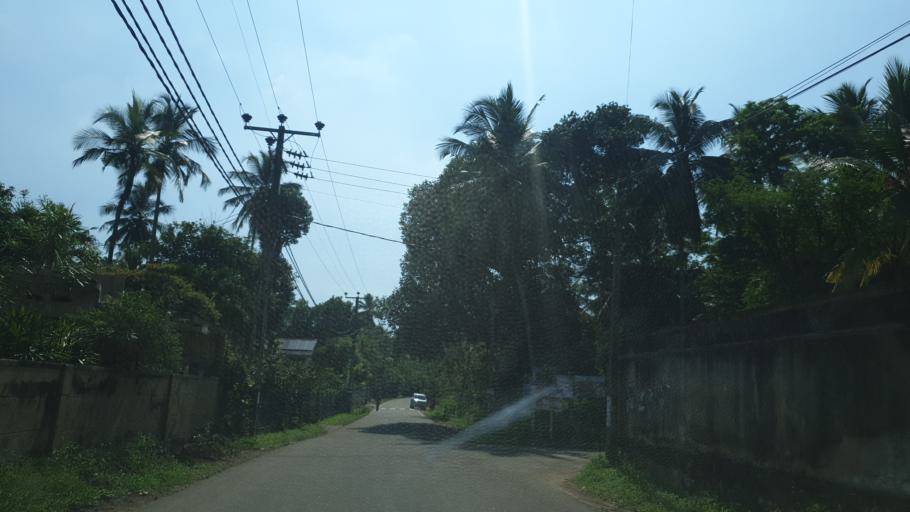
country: LK
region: Western
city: Moratuwa
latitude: 6.7647
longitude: 79.9306
